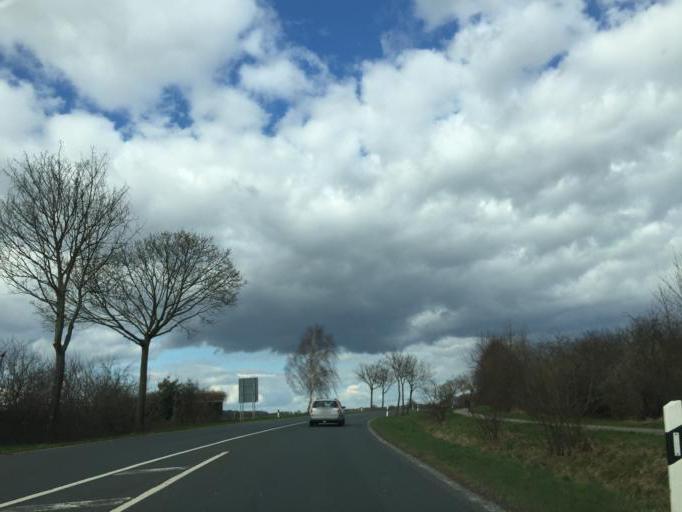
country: DE
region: Lower Saxony
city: Edemissen
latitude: 52.3887
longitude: 10.2587
